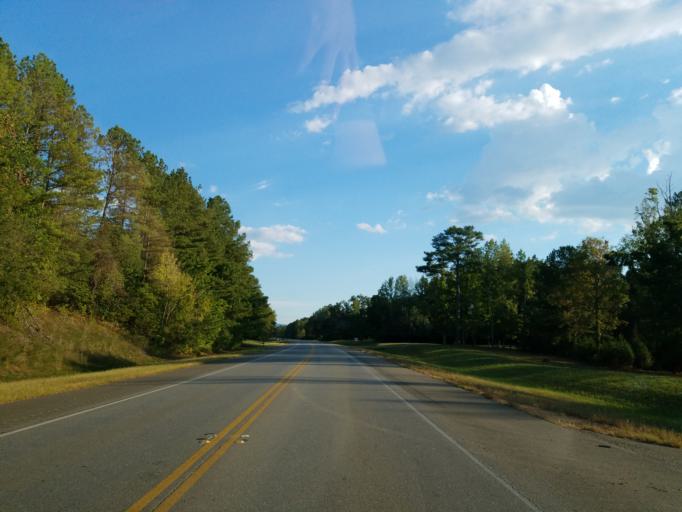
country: US
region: Georgia
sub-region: Murray County
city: Chatsworth
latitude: 34.6543
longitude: -84.7197
